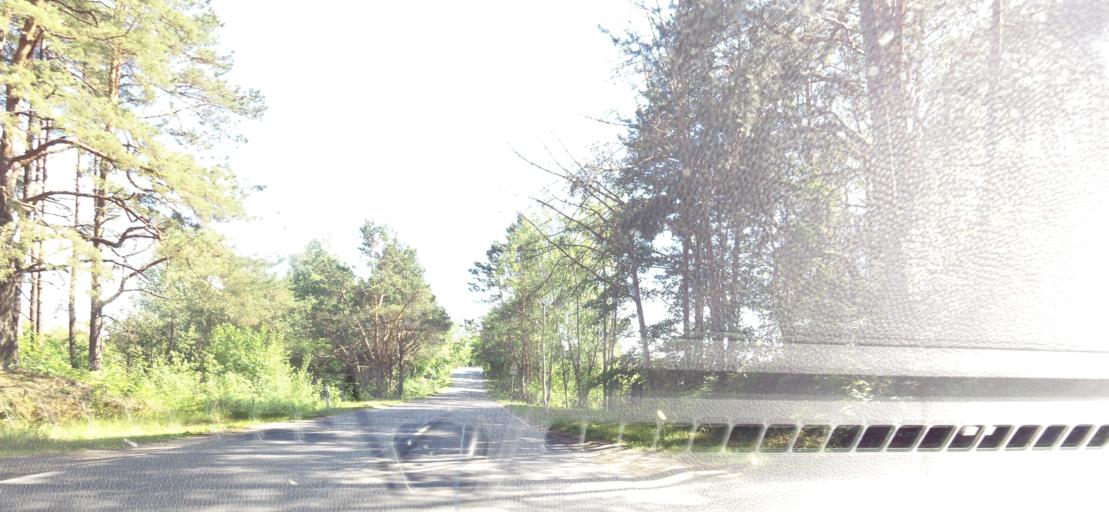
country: LT
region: Vilnius County
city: Rasos
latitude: 54.7937
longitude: 25.3506
